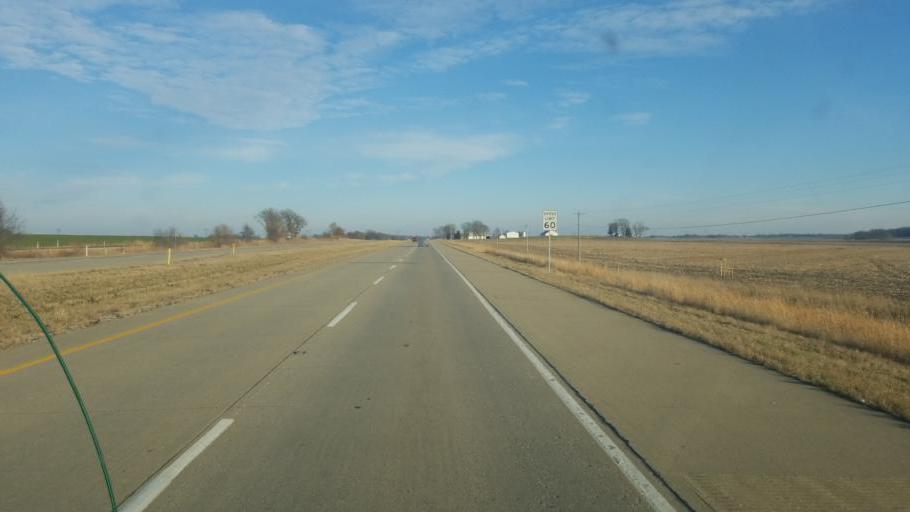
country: US
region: Indiana
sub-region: Knox County
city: Bicknell
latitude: 38.6745
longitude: -87.3665
